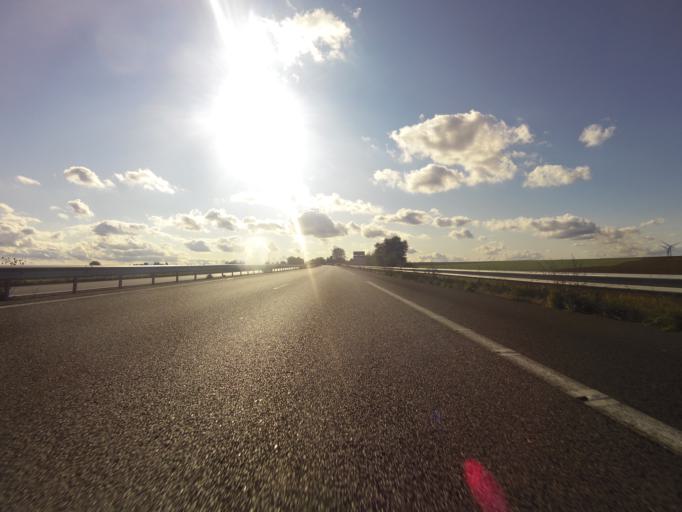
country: FR
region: Nord-Pas-de-Calais
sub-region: Departement du Pas-de-Calais
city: Bourlon
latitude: 50.1281
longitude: 3.0984
